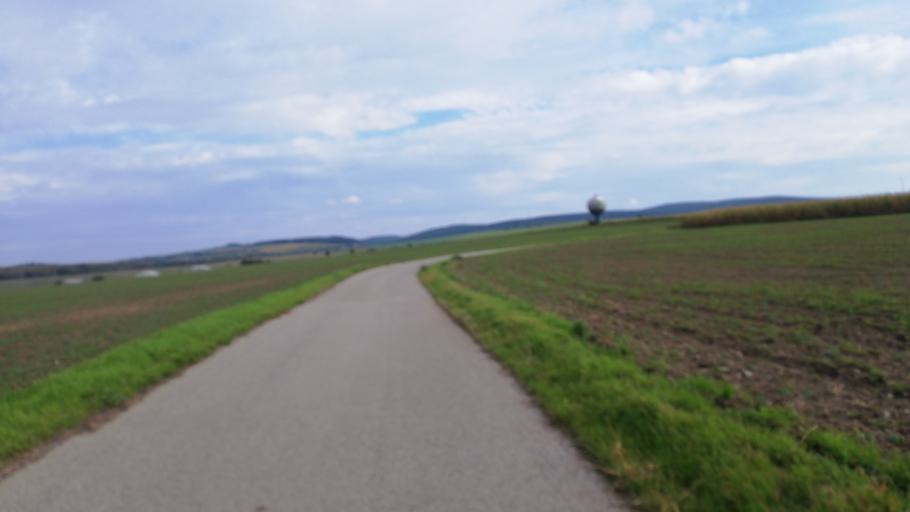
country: CZ
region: South Moravian
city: Sudomerice
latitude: 48.8490
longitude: 17.2644
